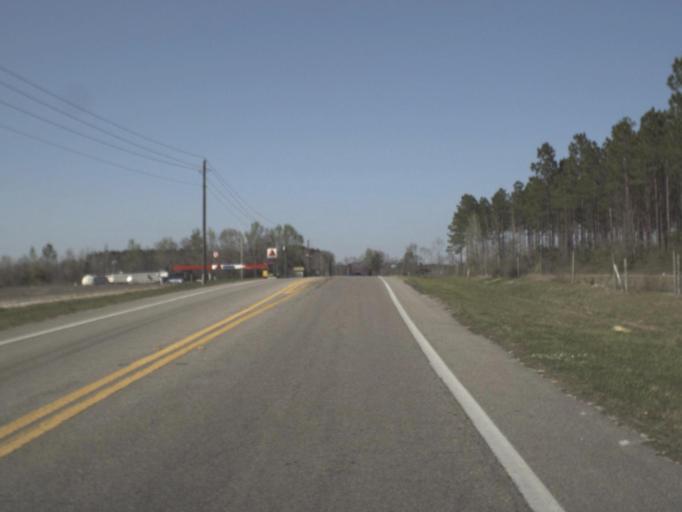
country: US
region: Florida
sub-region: Gulf County
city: Wewahitchka
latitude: 30.1541
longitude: -85.2094
